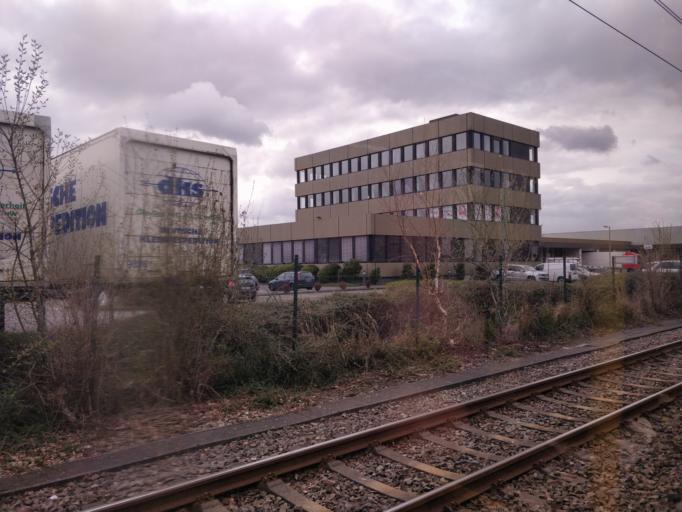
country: DE
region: North Rhine-Westphalia
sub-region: Regierungsbezirk Koln
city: Frechen
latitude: 50.9174
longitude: 6.8575
